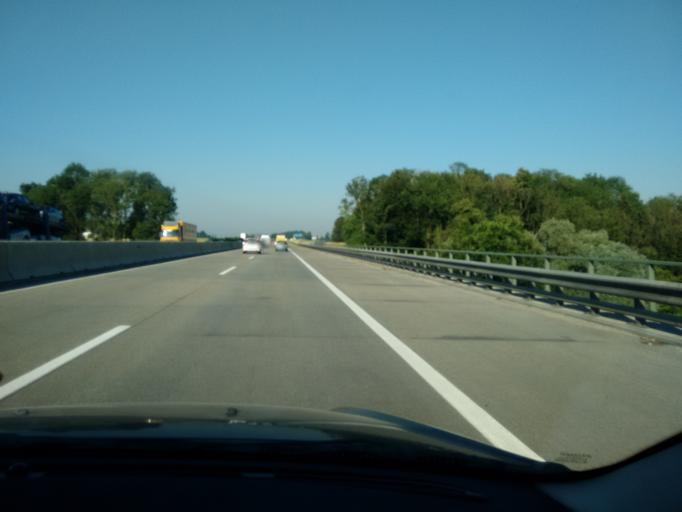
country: AT
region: Upper Austria
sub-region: Wels-Land
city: Sattledt
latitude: 48.0507
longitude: 14.0176
